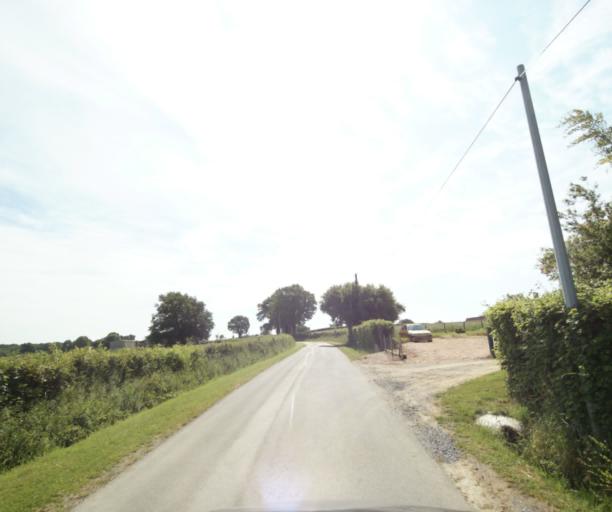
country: FR
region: Bourgogne
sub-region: Departement de Saone-et-Loire
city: Palinges
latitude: 46.5417
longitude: 4.1559
